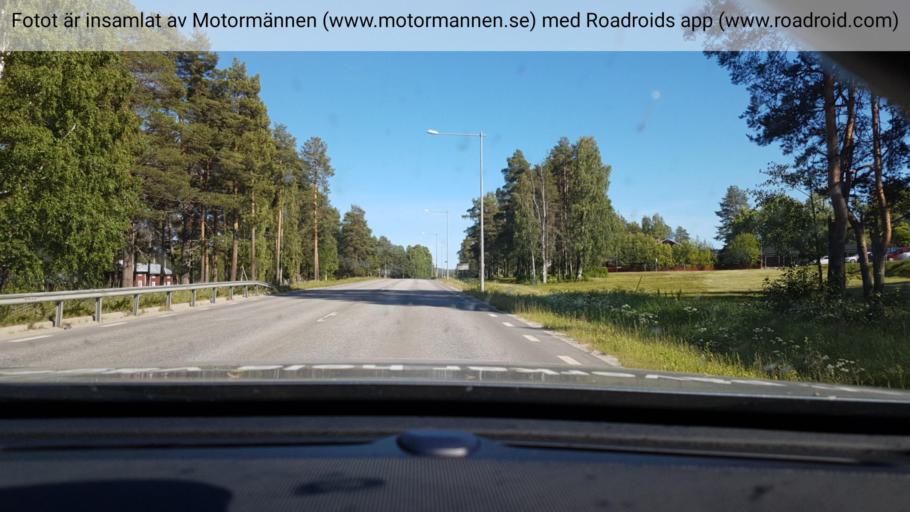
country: SE
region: Vaesterbotten
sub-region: Lycksele Kommun
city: Lycksele
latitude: 64.6046
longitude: 18.6664
